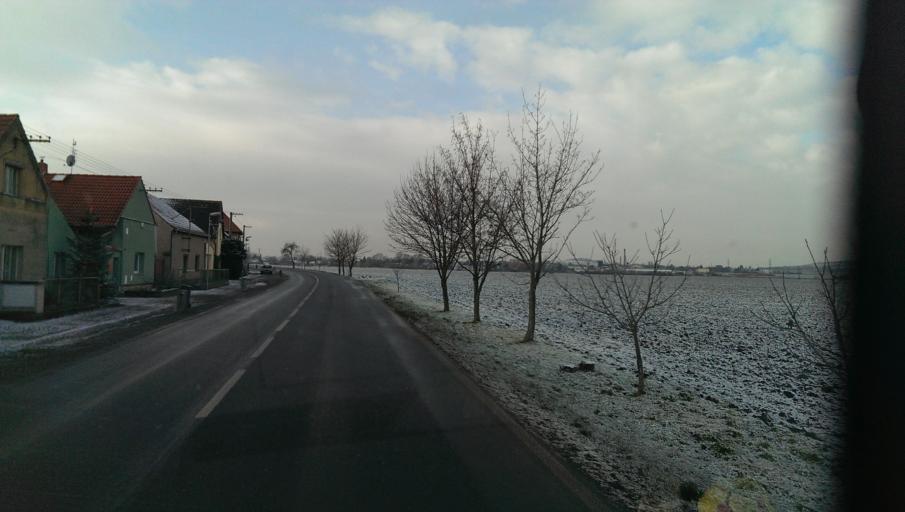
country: CZ
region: Ustecky
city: Libochovice
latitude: 50.4109
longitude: 14.0657
